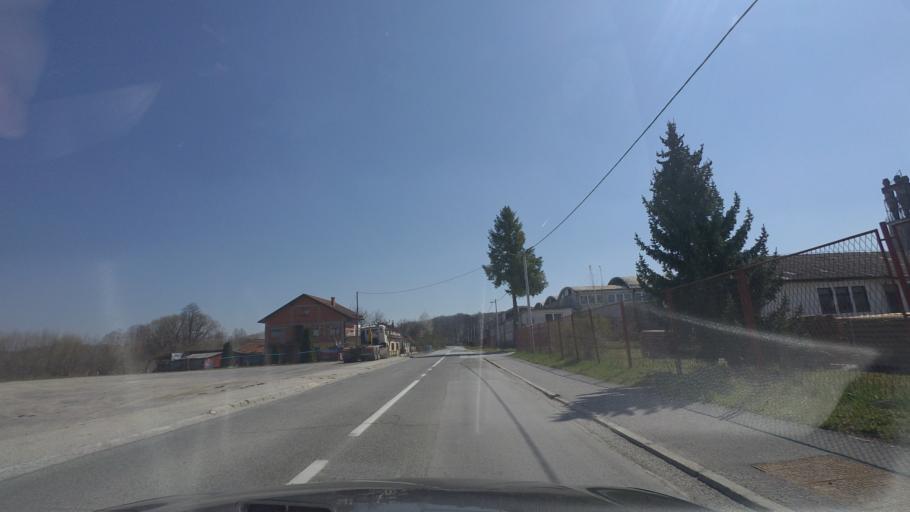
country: HR
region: Sisacko-Moslavacka
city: Gvozd
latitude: 45.3500
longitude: 15.8665
